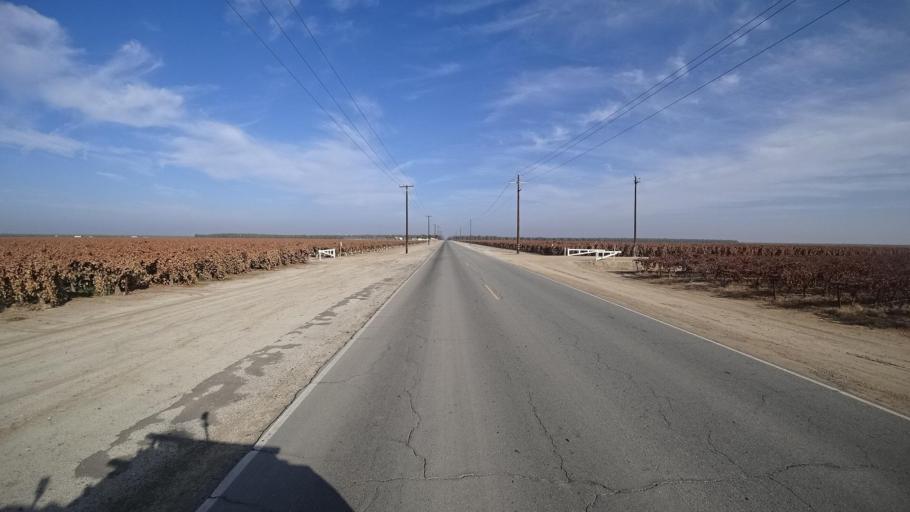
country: US
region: California
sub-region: Kern County
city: McFarland
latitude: 35.6091
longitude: -119.2044
